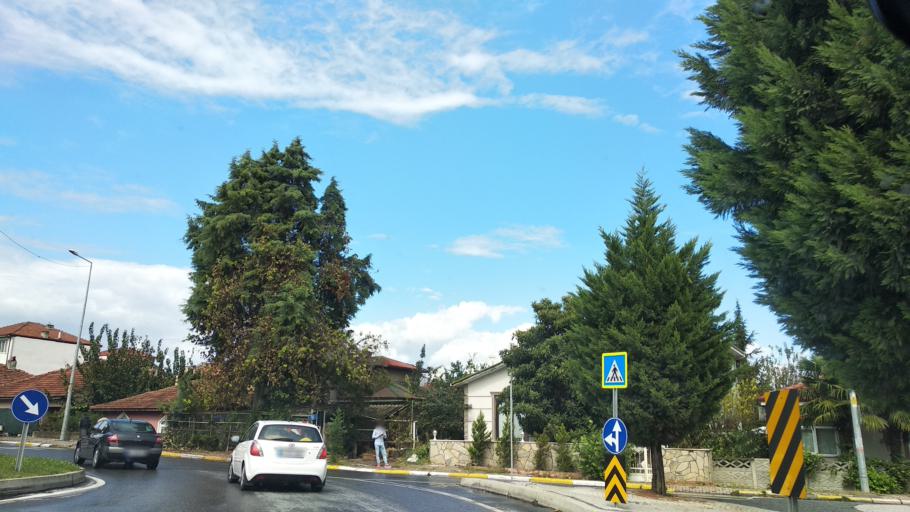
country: TR
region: Sakarya
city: Adapazari
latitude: 40.7574
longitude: 30.3737
